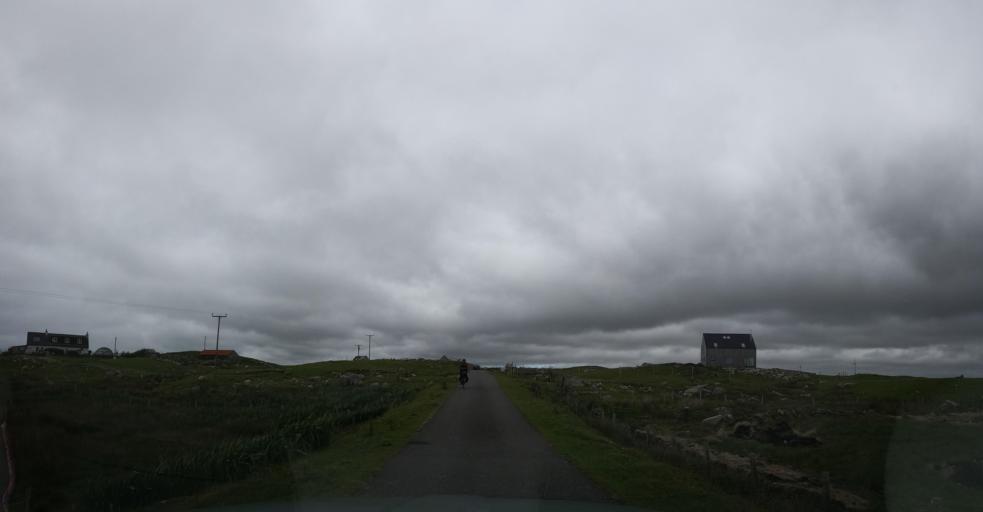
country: GB
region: Scotland
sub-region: Eilean Siar
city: Isle of North Uist
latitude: 57.5446
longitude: -7.3438
